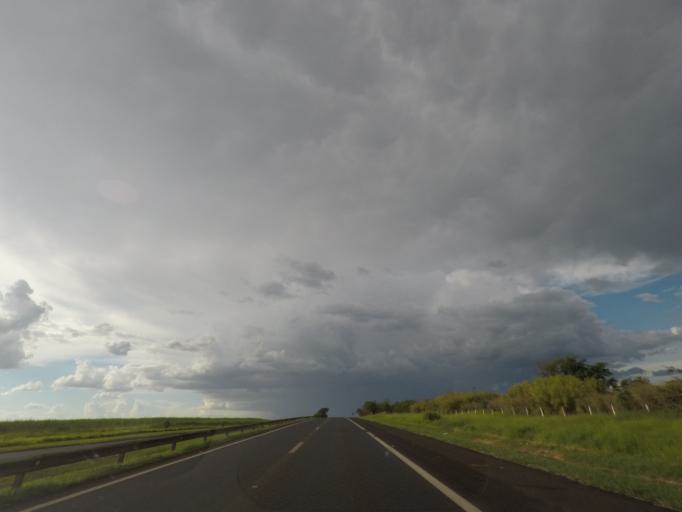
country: BR
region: Sao Paulo
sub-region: Jardinopolis
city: Jardinopolis
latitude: -21.0184
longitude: -47.8412
